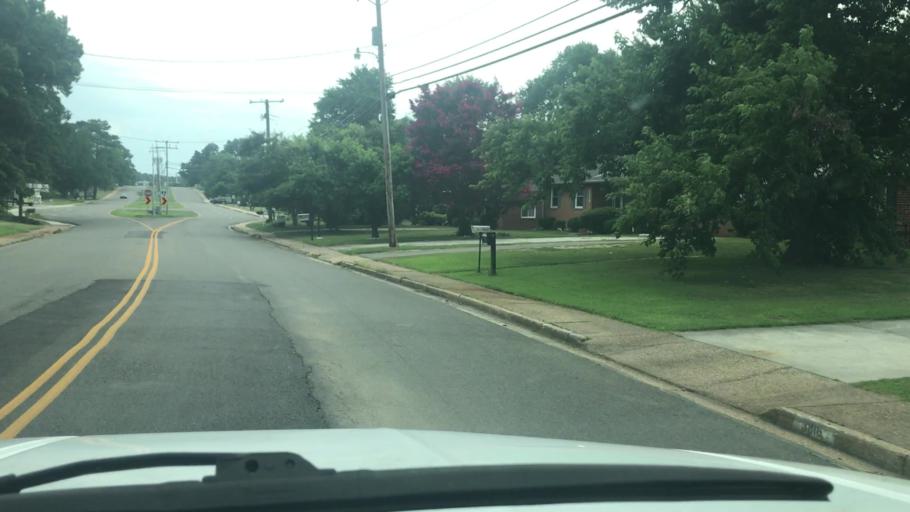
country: US
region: Virginia
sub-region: Henrico County
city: Laurel
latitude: 37.6414
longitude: -77.5442
